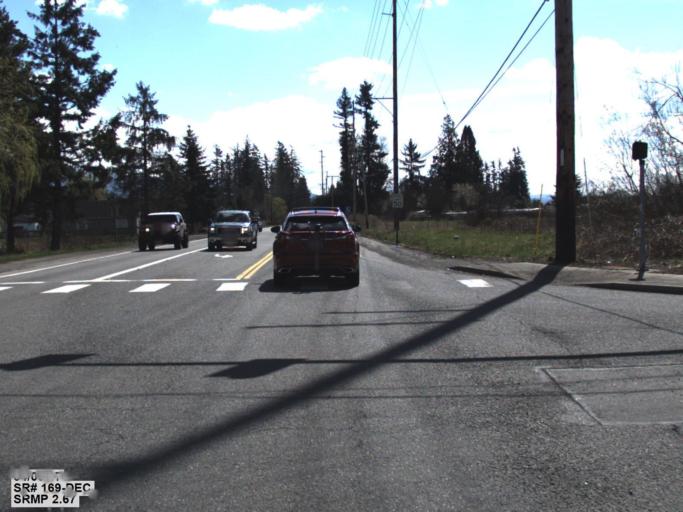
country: US
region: Washington
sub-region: King County
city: Enumclaw
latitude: 47.2428
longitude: -121.9898
